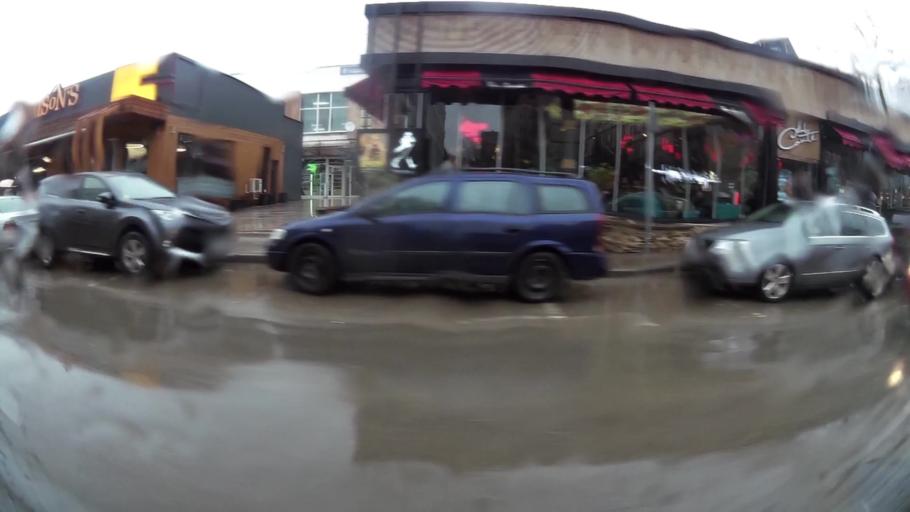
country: BG
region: Sofia-Capital
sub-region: Stolichna Obshtina
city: Sofia
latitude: 42.6537
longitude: 23.3446
